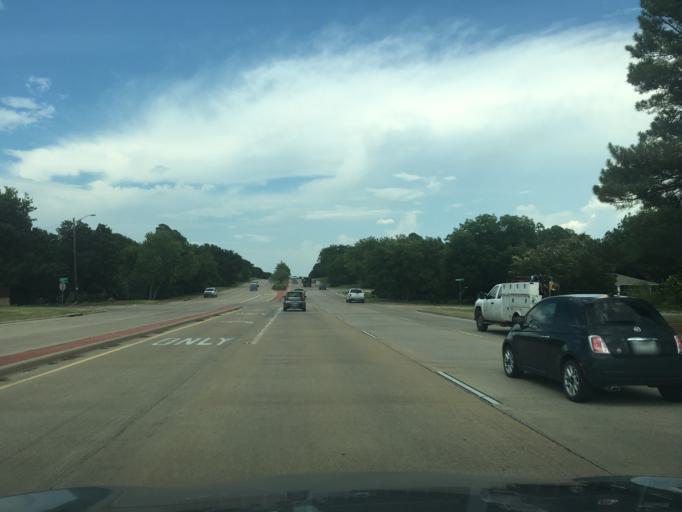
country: US
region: Texas
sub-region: Denton County
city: Denton
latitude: 33.2341
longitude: -97.1126
